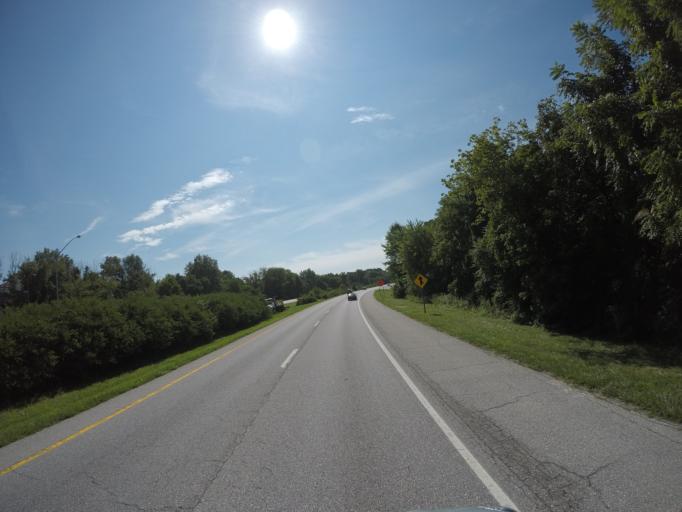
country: US
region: Maryland
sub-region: Howard County
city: Columbia
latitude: 39.2241
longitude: -76.8426
